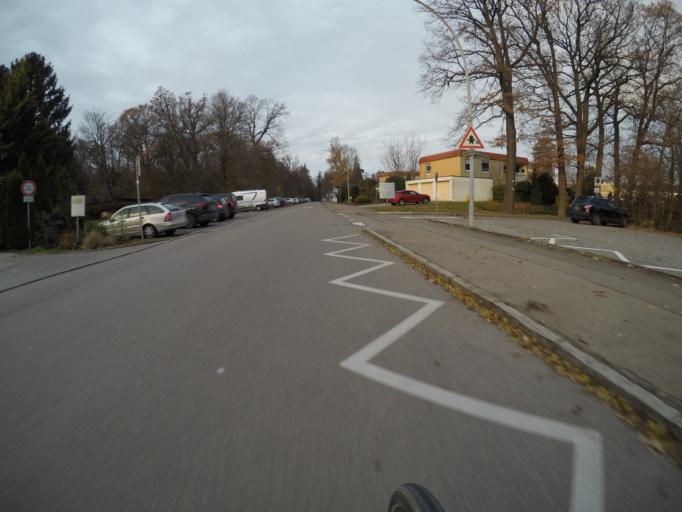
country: DE
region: Baden-Wuerttemberg
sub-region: Regierungsbezirk Stuttgart
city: Ostfildern
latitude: 48.7398
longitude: 9.2531
